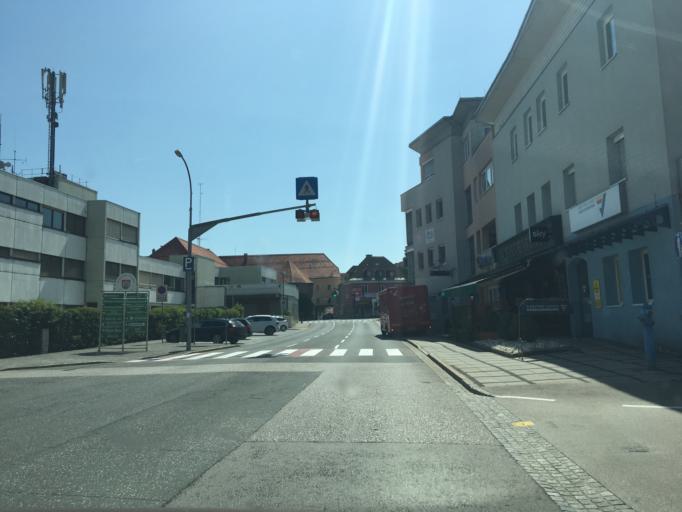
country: AT
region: Carinthia
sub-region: Politischer Bezirk Volkermarkt
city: Voelkermarkt
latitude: 46.6622
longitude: 14.6334
